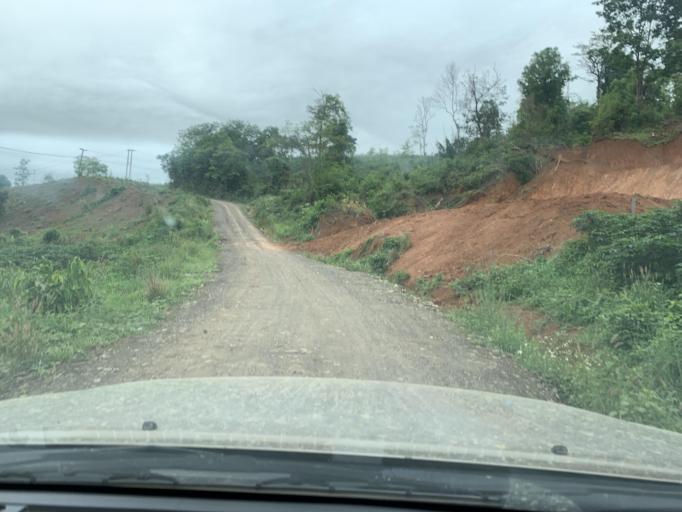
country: TH
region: Nan
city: Mae Charim
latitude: 18.4168
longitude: 101.4562
